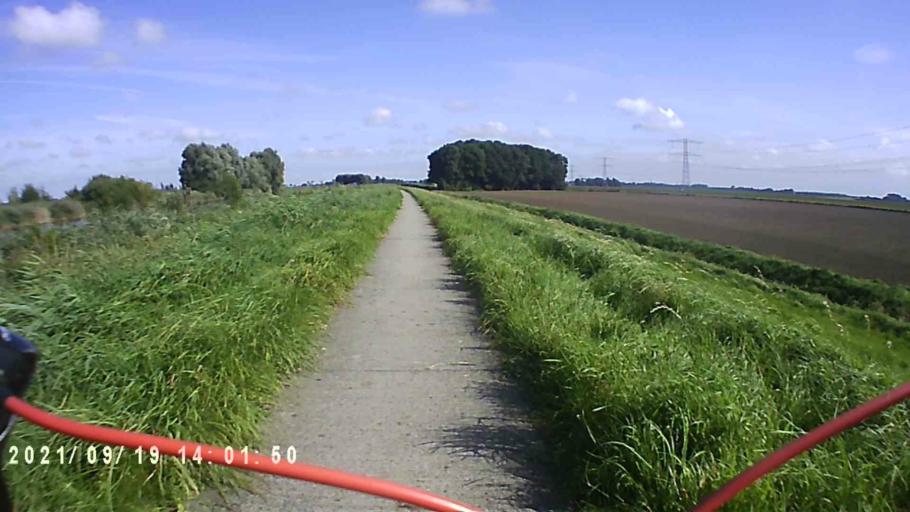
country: NL
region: Groningen
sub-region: Gemeente  Oldambt
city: Winschoten
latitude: 53.1448
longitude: 7.1089
